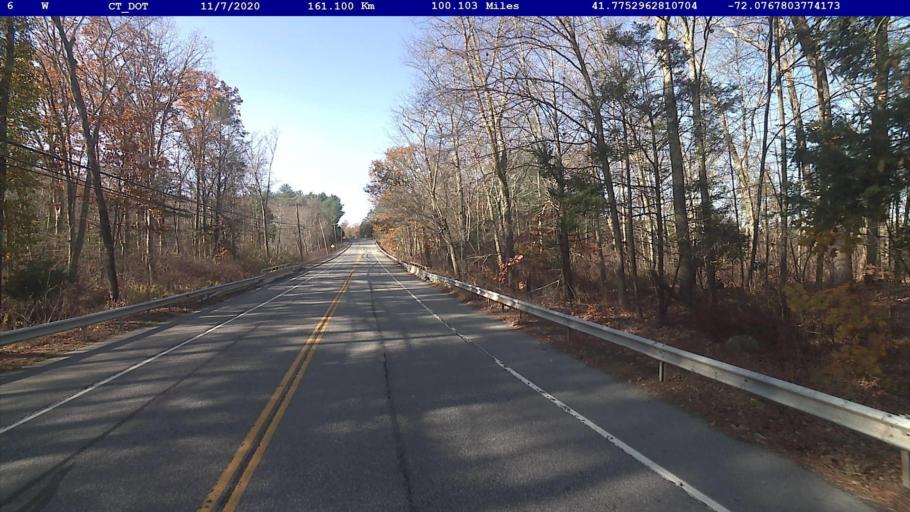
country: US
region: Connecticut
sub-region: Windham County
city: Windham
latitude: 41.7753
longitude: -72.0768
